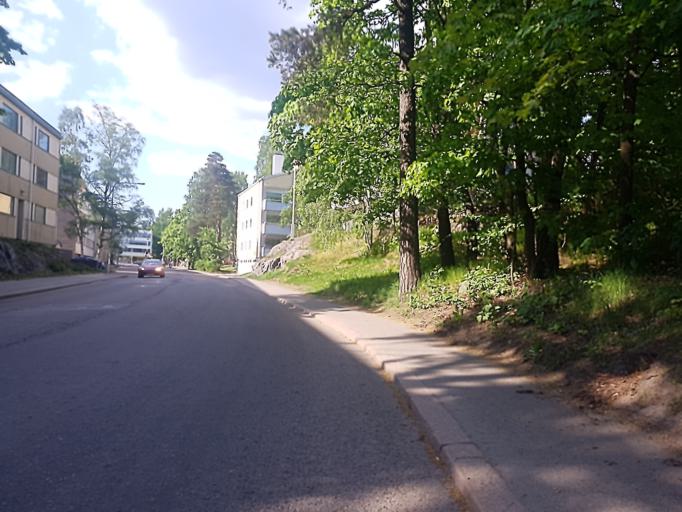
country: FI
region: Uusimaa
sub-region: Helsinki
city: Helsinki
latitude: 60.2140
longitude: 24.8991
